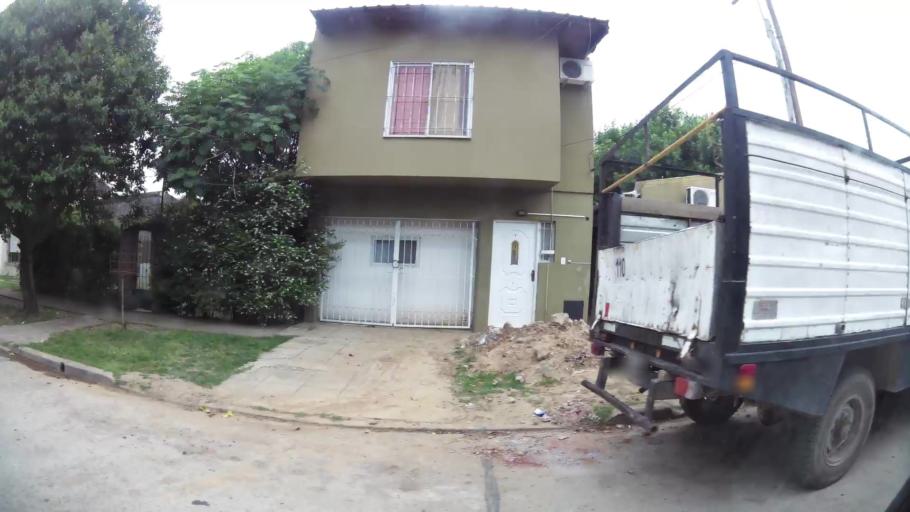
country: AR
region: Buenos Aires
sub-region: Partido de Campana
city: Campana
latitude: -34.1829
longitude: -58.9474
